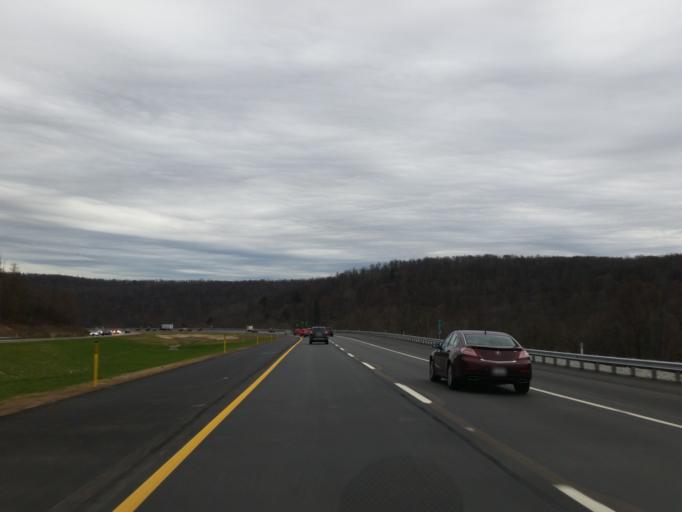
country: US
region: Pennsylvania
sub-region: Somerset County
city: Somerset
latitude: 40.0950
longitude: -79.2027
